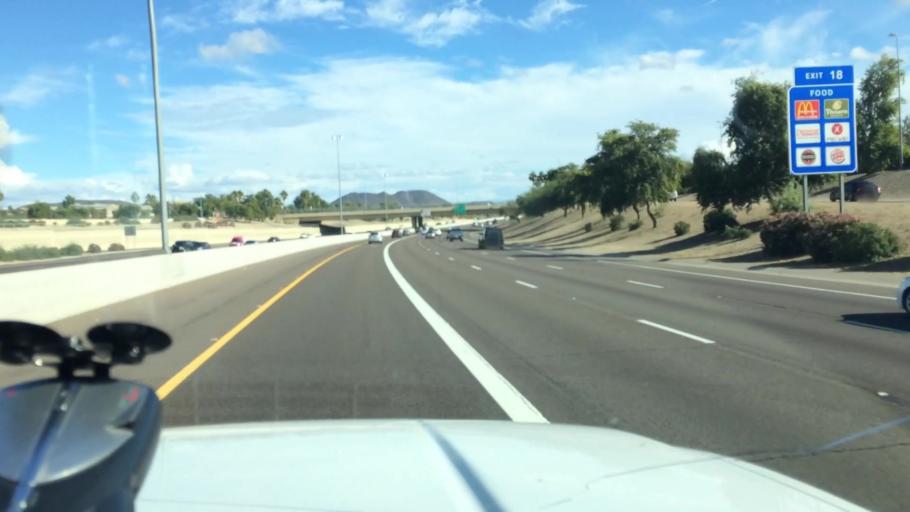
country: US
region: Arizona
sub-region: Maricopa County
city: Sun City
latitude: 33.6671
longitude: -112.2234
